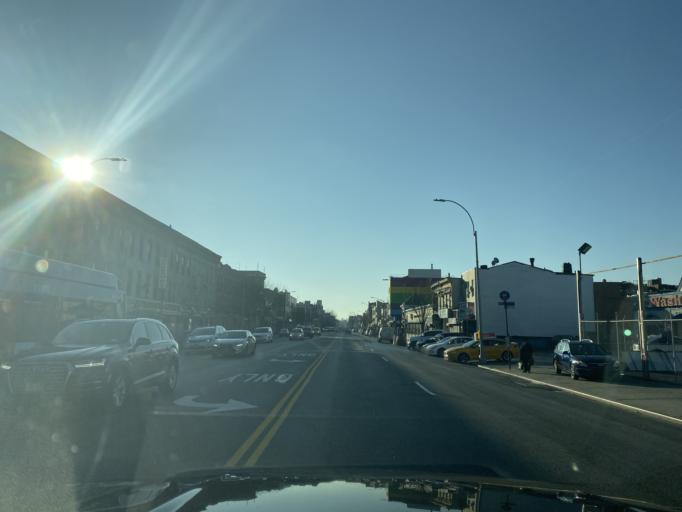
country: US
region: New York
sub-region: Kings County
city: Brooklyn
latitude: 40.6412
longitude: -73.9694
